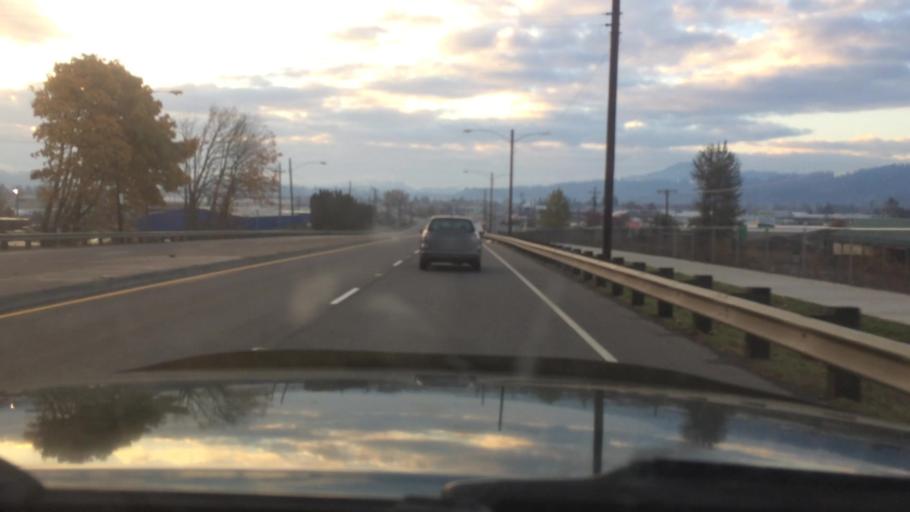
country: US
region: Oregon
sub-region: Lane County
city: Eugene
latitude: 44.0593
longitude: -123.1328
